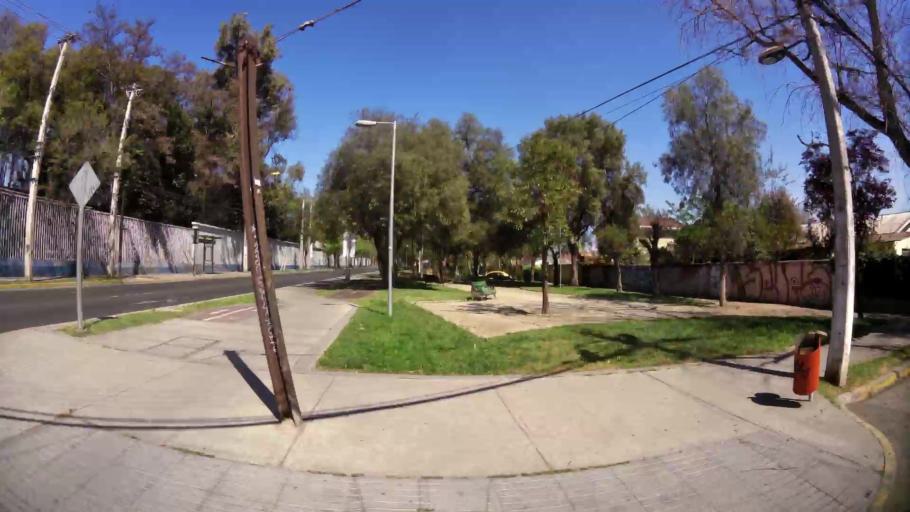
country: CL
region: Santiago Metropolitan
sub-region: Provincia de Santiago
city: Lo Prado
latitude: -33.5189
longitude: -70.7557
